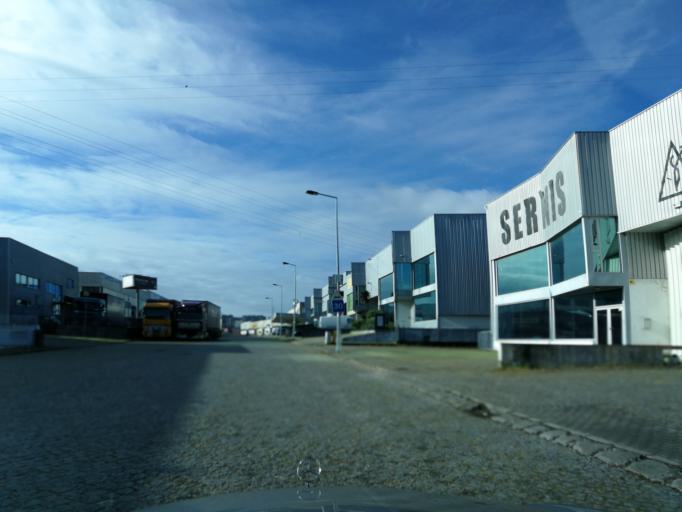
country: PT
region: Braga
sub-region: Braga
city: Braga
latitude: 41.5651
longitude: -8.4455
